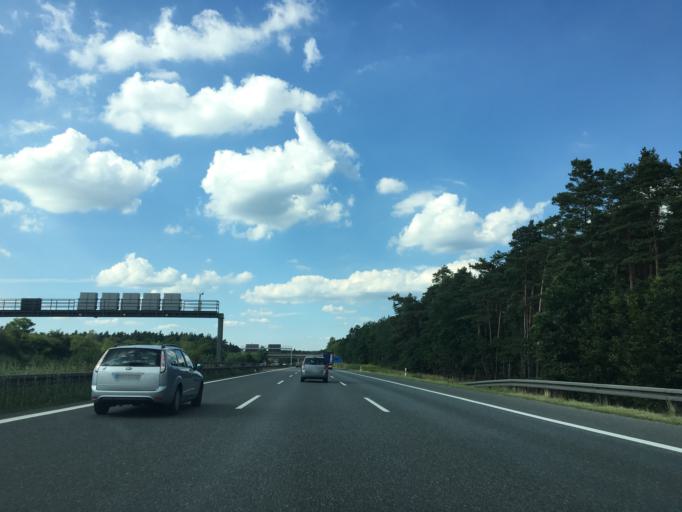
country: DE
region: Bavaria
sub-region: Regierungsbezirk Mittelfranken
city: Feucht
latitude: 49.3623
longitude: 11.2025
